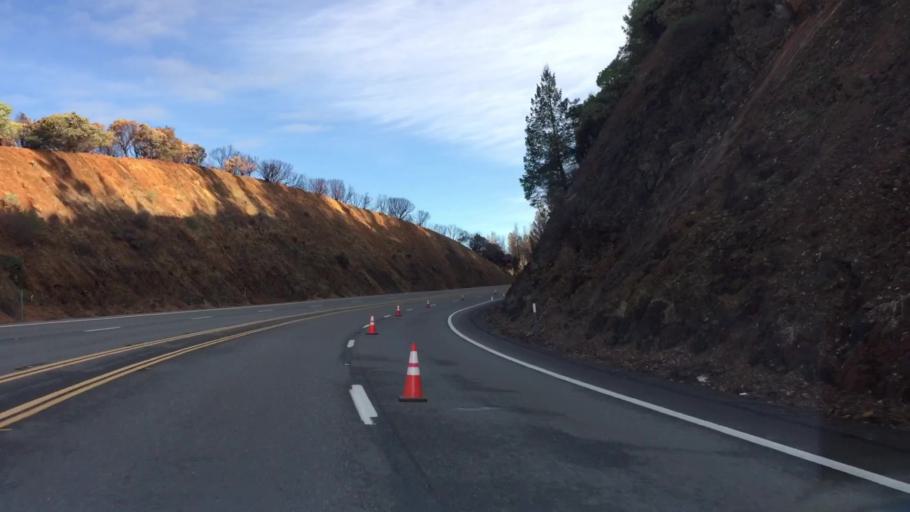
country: US
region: California
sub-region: Butte County
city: Paradise
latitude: 39.7087
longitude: -121.5302
